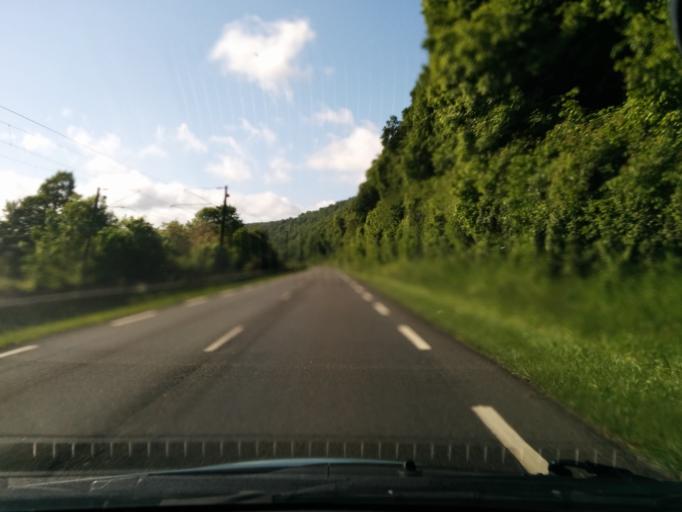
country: FR
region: Ile-de-France
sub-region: Departement des Yvelines
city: Limetz-Villez
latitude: 49.0525
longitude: 1.5278
